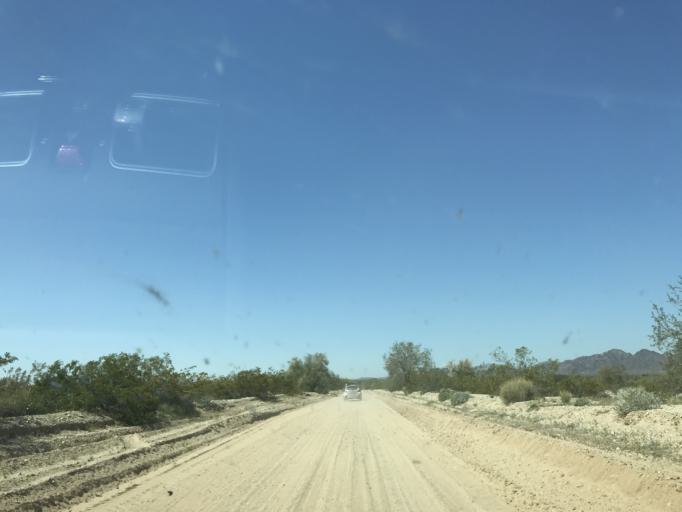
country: US
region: California
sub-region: Riverside County
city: Mesa Verde
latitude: 33.4919
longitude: -114.8847
